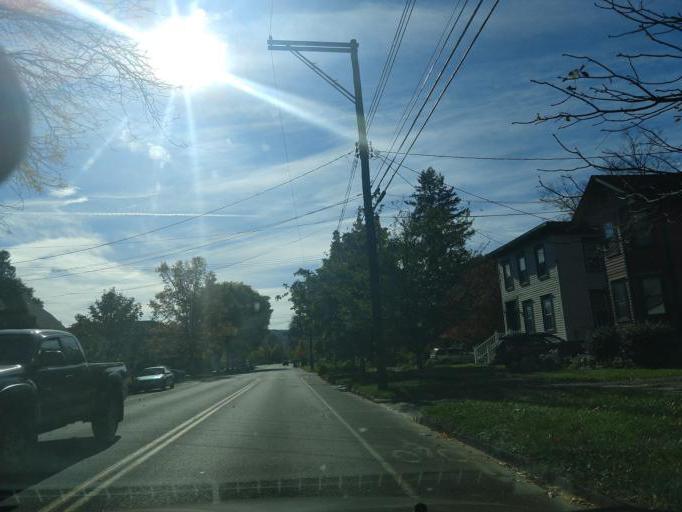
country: US
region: New York
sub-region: Tompkins County
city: Ithaca
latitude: 42.4465
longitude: -76.4994
